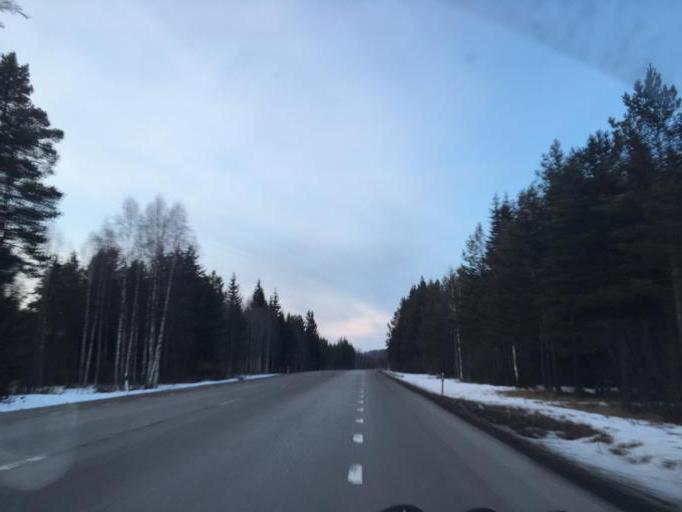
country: SE
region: Dalarna
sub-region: Leksand Municipality
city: Leksand
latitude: 60.7695
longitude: 15.0184
